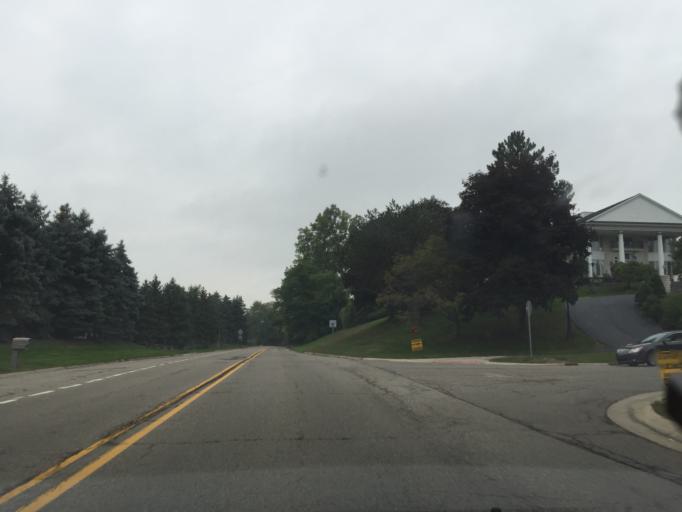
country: US
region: Michigan
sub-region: Oakland County
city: Orchard Lake
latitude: 42.5688
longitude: -83.3234
